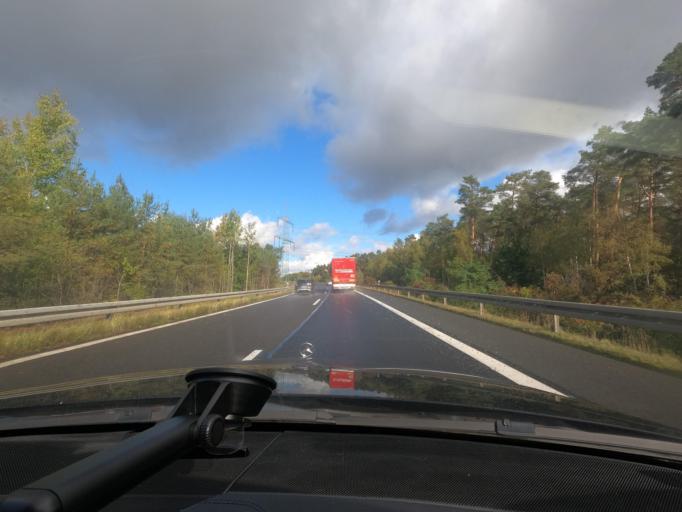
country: DE
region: Brandenburg
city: Fichtenwalde
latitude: 52.2856
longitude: 12.9184
